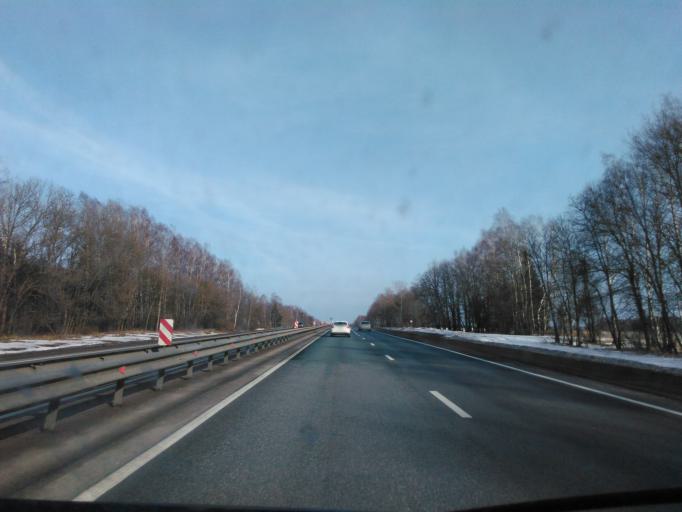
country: RU
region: Smolensk
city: Kholm-Zhirkovskiy
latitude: 55.1844
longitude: 33.7045
